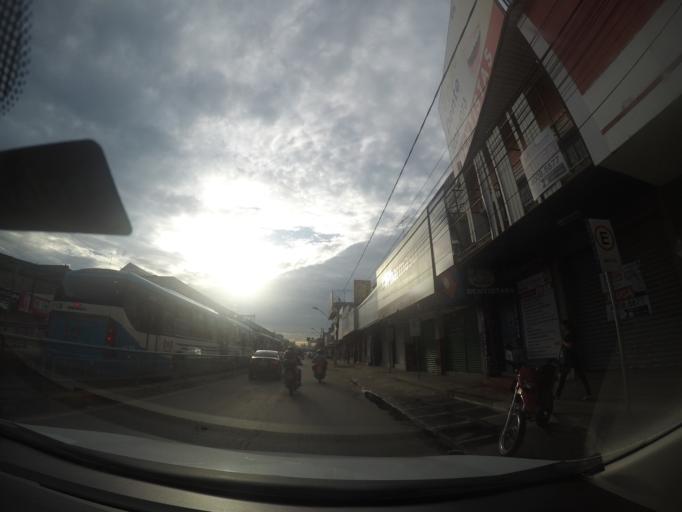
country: BR
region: Goias
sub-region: Goiania
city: Goiania
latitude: -16.6725
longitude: -49.2898
